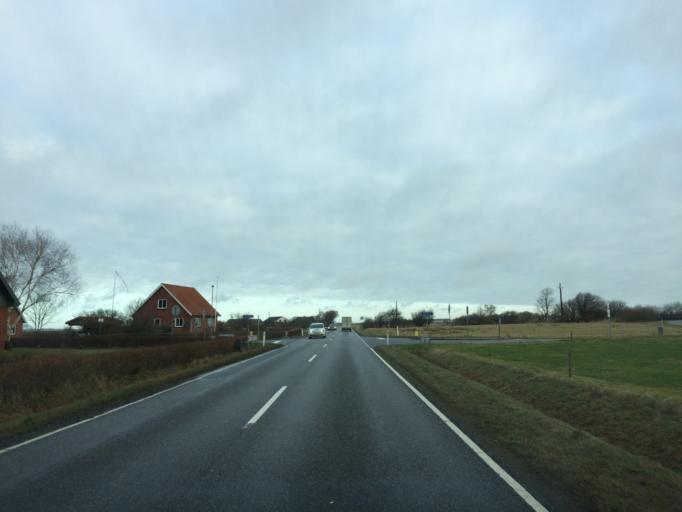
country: DK
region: Central Jutland
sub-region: Struer Kommune
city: Struer
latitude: 56.4309
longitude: 8.5153
